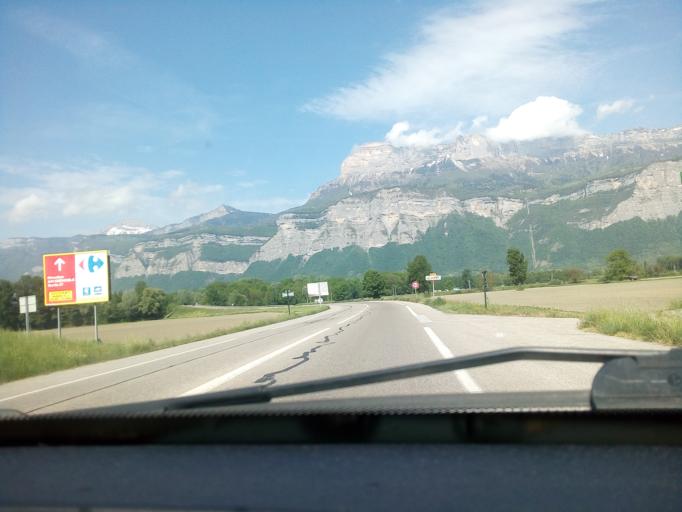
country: FR
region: Rhone-Alpes
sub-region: Departement de l'Isere
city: Le Champ-pres-Froges
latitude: 45.2805
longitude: 5.9299
